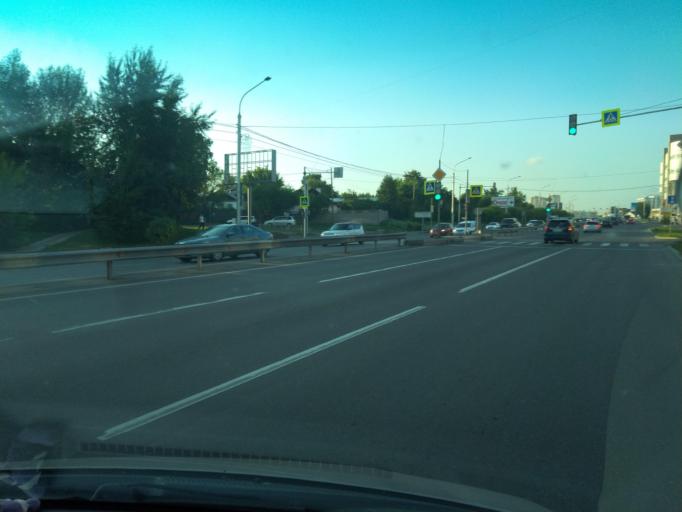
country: RU
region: Krasnoyarskiy
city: Krasnoyarsk
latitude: 56.0270
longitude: 92.8878
